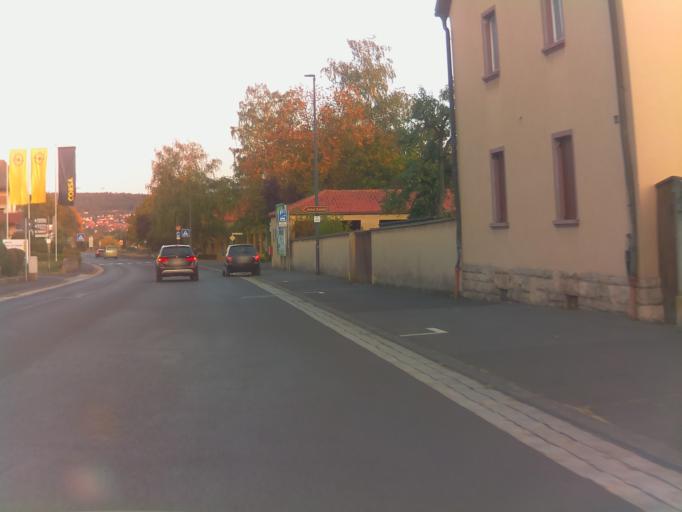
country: DE
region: Bavaria
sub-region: Regierungsbezirk Unterfranken
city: Hammelburg
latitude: 50.1149
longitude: 9.8983
